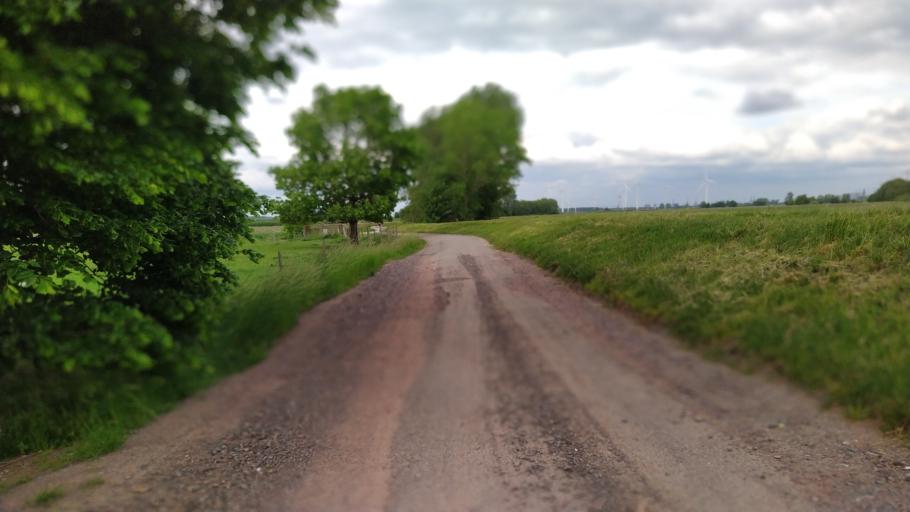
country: DE
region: Lower Saxony
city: Neu Wulmstorf
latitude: 53.4940
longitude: 9.8185
